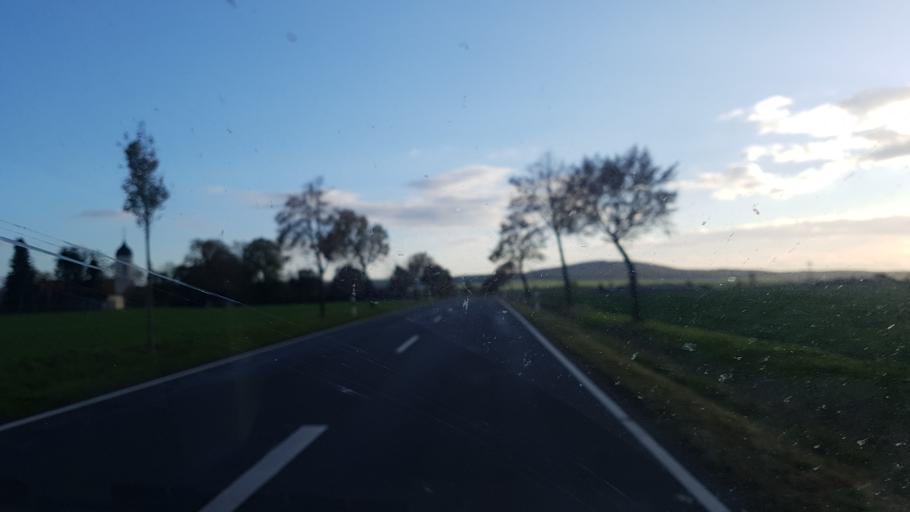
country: DE
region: Saxony
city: Dahlen
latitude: 51.3417
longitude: 13.0310
